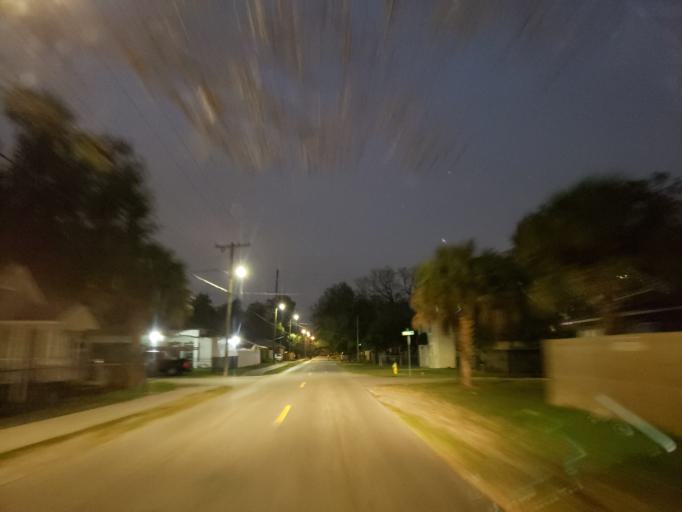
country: US
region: Florida
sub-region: Hillsborough County
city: University
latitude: 28.0226
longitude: -82.4429
